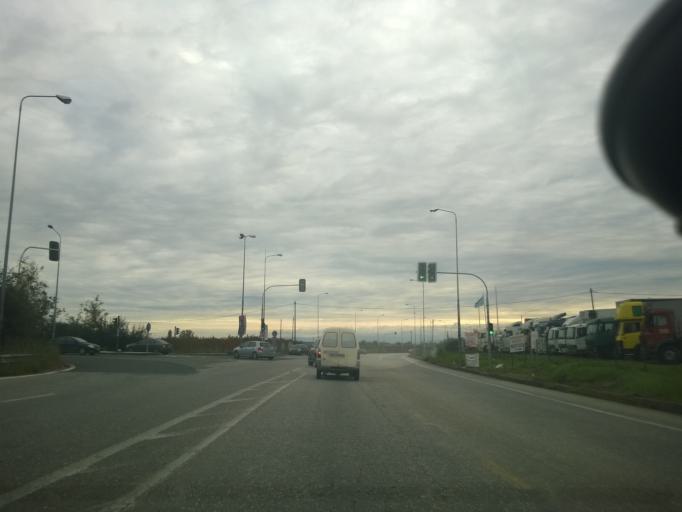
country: GR
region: Central Macedonia
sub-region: Nomos Pellis
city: Mavrovouni
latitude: 40.7884
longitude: 22.1597
